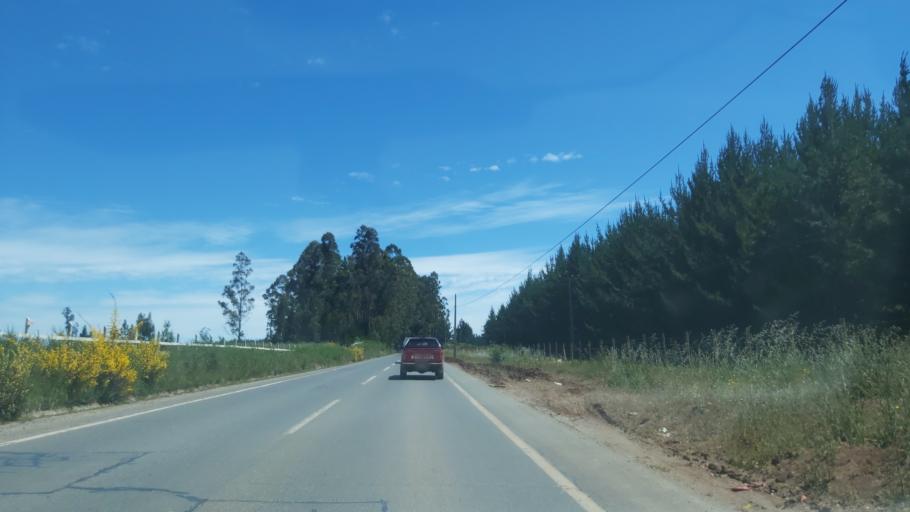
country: CL
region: Maule
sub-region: Provincia de Talca
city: Constitucion
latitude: -35.3954
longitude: -72.4295
